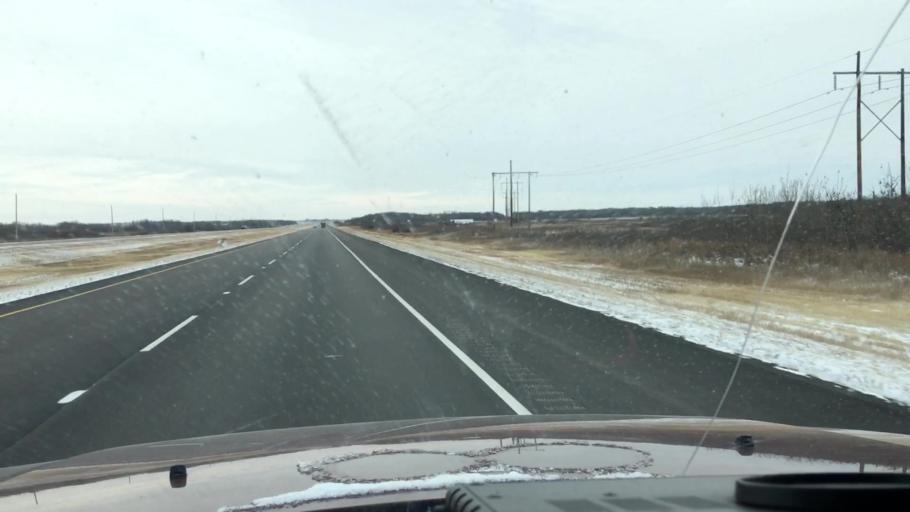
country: CA
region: Saskatchewan
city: Saskatoon
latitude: 51.8890
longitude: -106.5163
